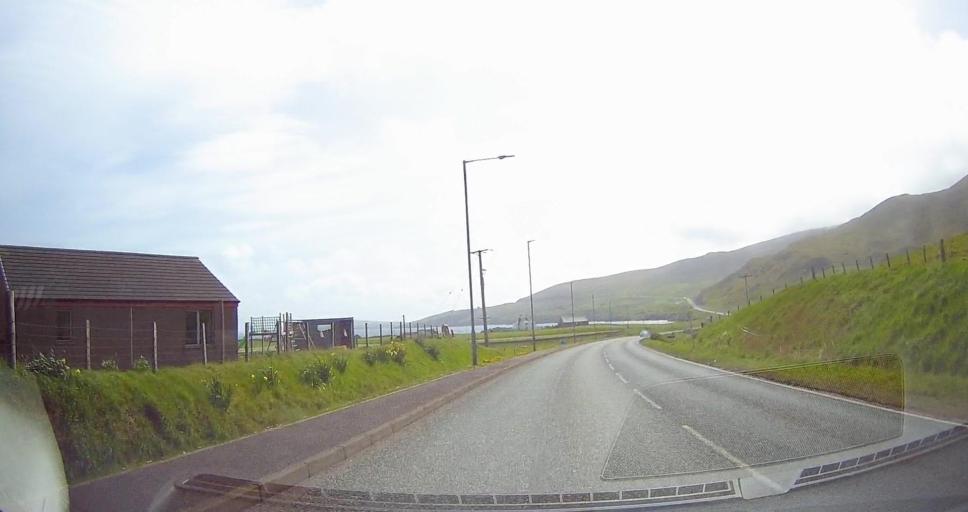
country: GB
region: Scotland
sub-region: Shetland Islands
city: Sandwick
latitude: 60.0385
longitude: -1.2295
